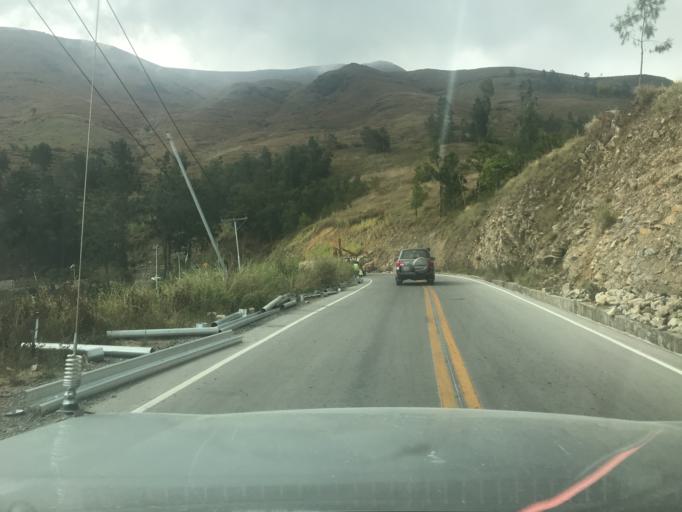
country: TL
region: Manufahi
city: Same
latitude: -8.8919
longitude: 125.5963
